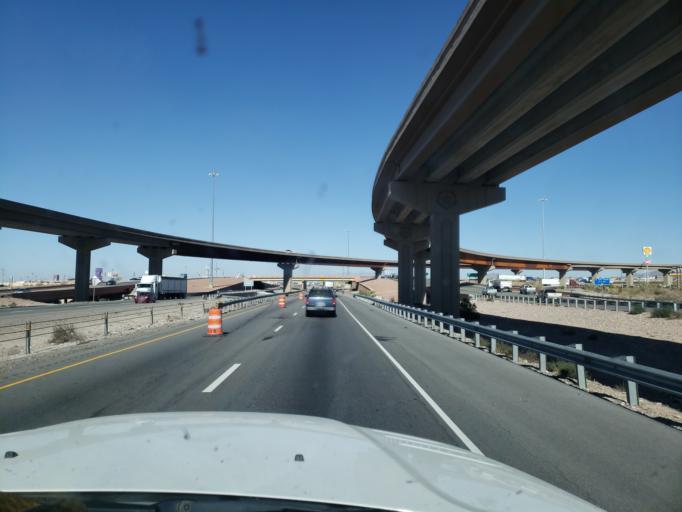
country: US
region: Texas
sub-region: El Paso County
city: Canutillo
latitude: 31.9054
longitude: -106.5827
